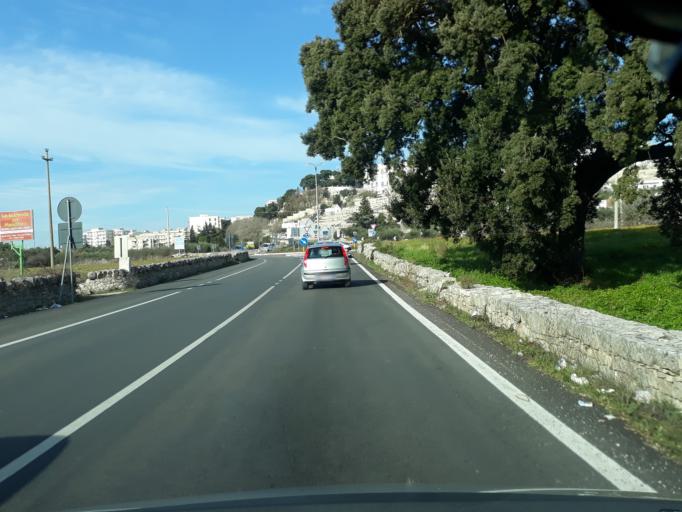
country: IT
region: Apulia
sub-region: Provincia di Bari
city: Locorotondo
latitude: 40.7483
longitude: 17.3299
